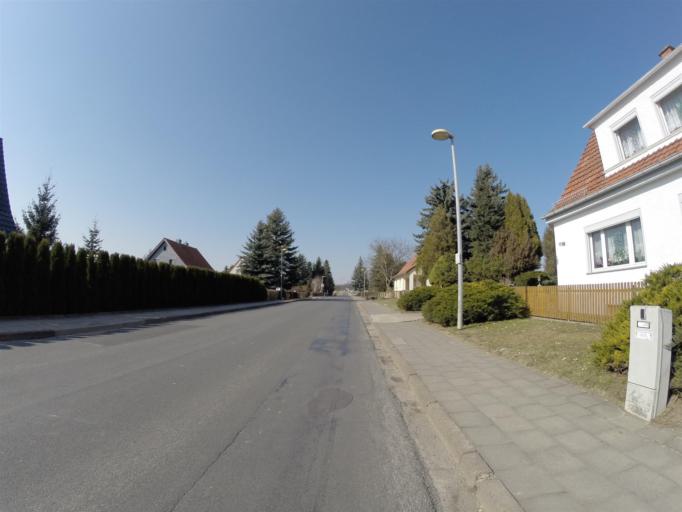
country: DE
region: Thuringia
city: Mellingen
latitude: 50.9462
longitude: 11.3903
